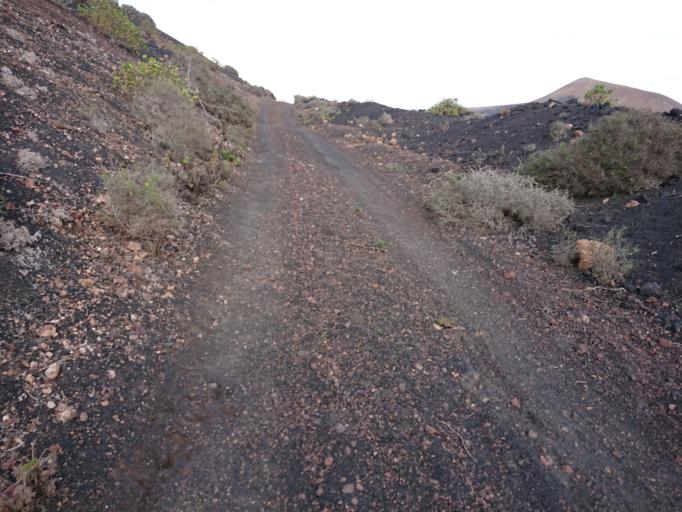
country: ES
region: Canary Islands
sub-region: Provincia de Las Palmas
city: Tinajo
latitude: 29.0120
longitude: -13.6934
